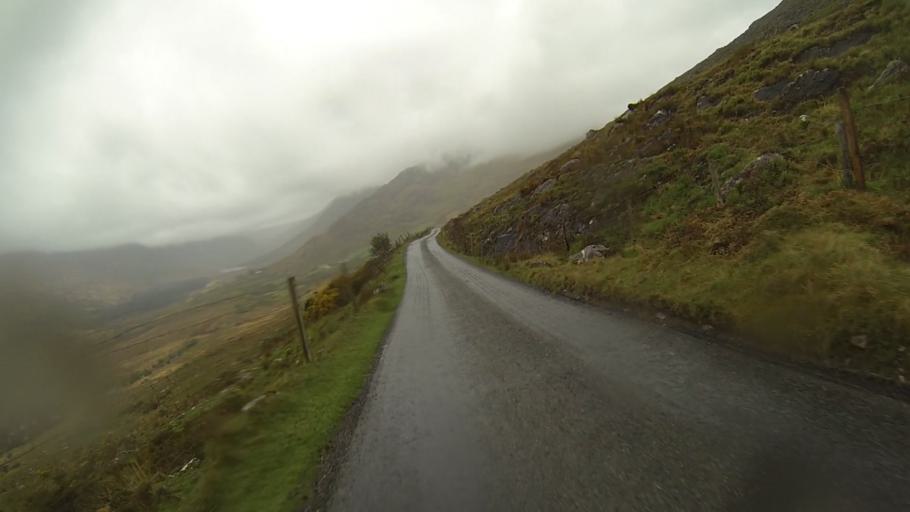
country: IE
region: Munster
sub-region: Ciarrai
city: Kenmare
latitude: 51.9896
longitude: -9.6504
